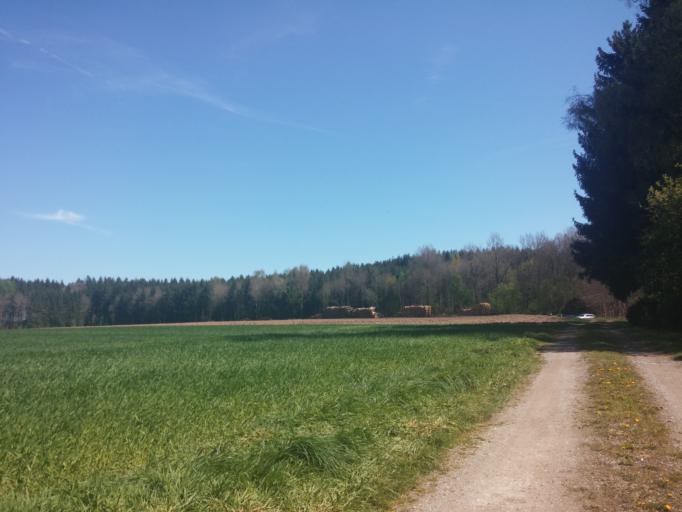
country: DE
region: Baden-Wuerttemberg
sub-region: Tuebingen Region
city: Aitrach
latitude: 47.9409
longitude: 10.1100
